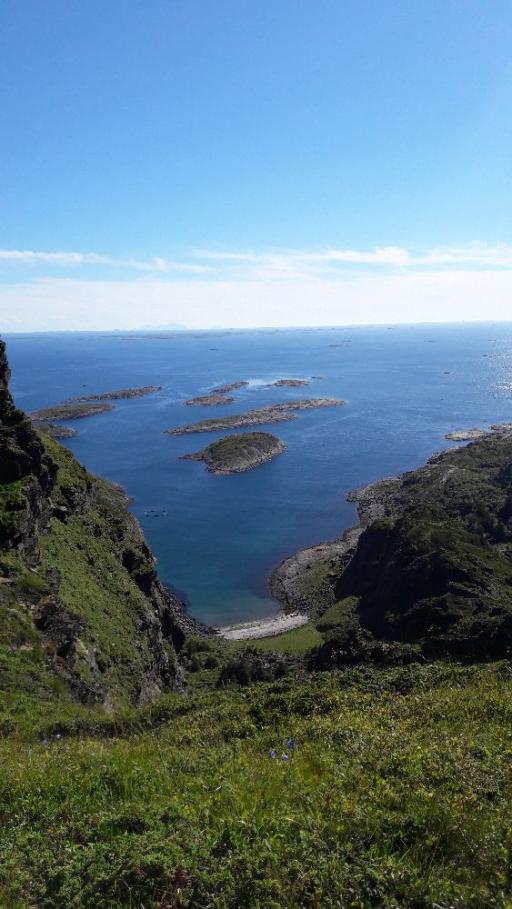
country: NO
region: Nordland
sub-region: Donna
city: Solfjellsjoen
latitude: 66.3611
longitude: 12.3531
